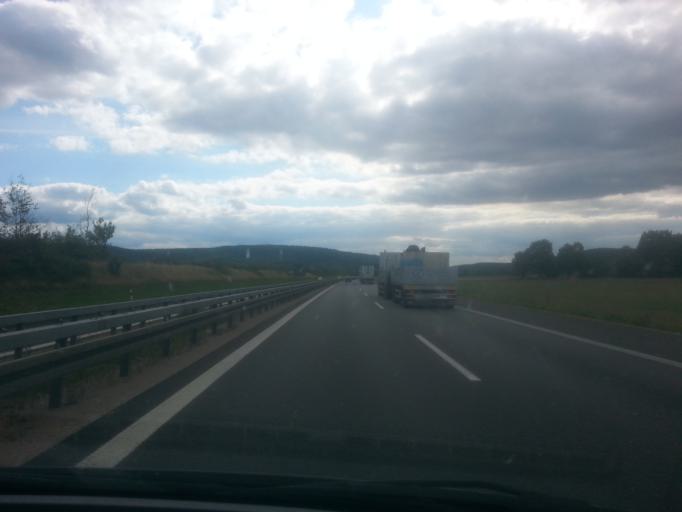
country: DE
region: Bavaria
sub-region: Upper Palatinate
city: Nabburg
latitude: 49.4474
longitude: 12.1908
